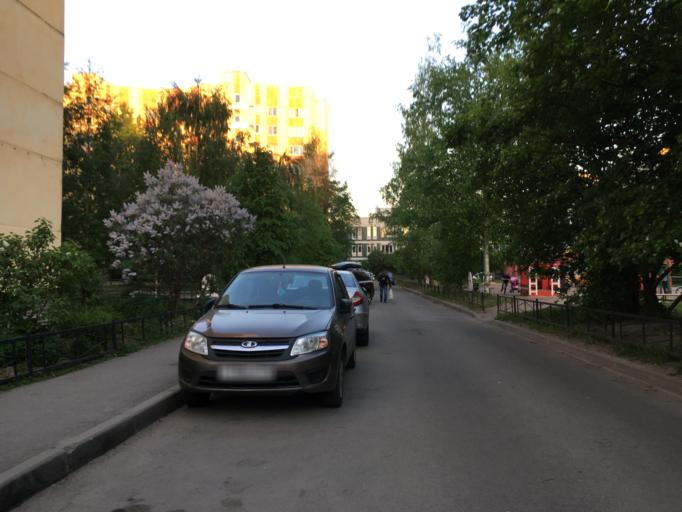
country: RU
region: St.-Petersburg
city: Komendantsky aerodrom
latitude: 60.0139
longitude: 30.2578
